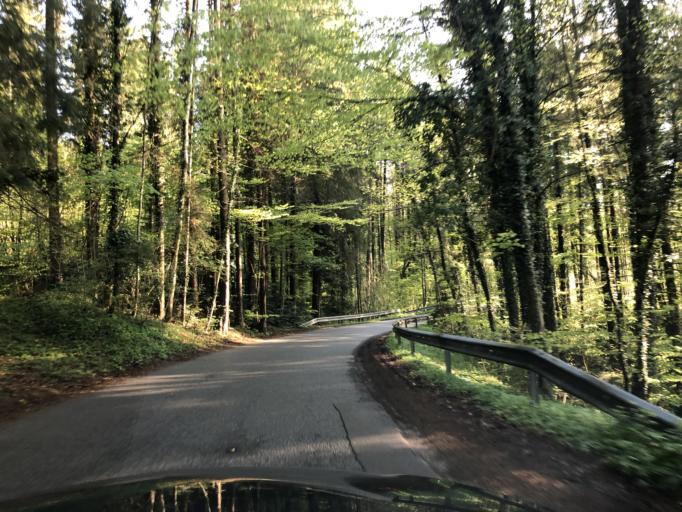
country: DE
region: Bavaria
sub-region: Upper Bavaria
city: Samerberg
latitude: 47.7992
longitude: 12.2280
